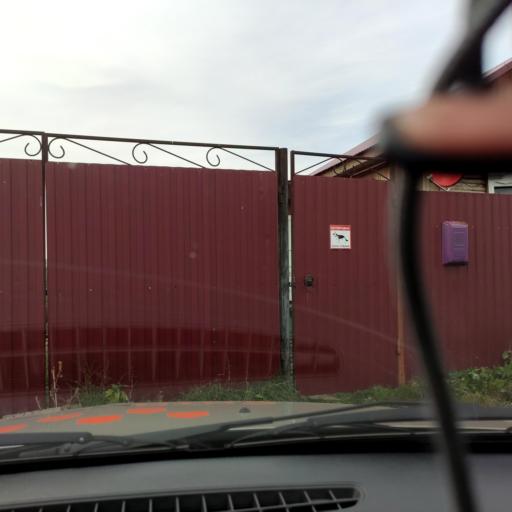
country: RU
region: Bashkortostan
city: Kabakovo
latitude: 54.5294
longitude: 56.0246
